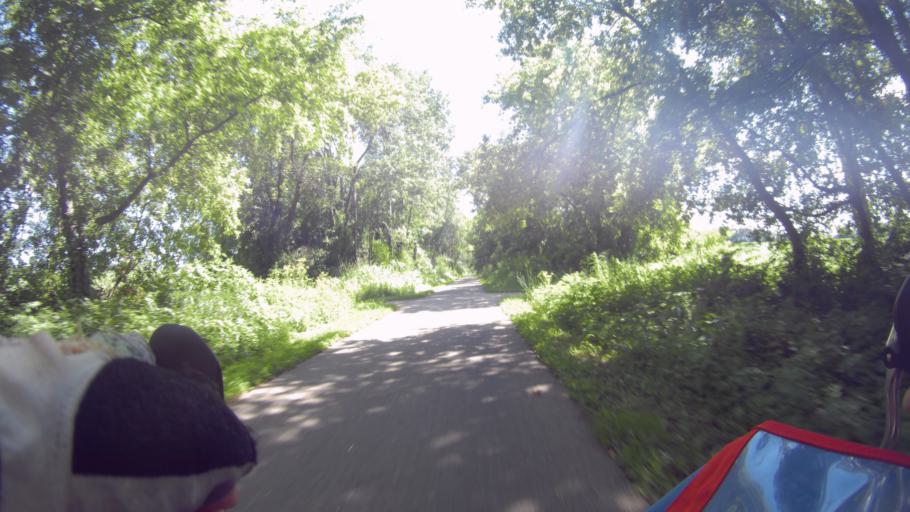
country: US
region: Wisconsin
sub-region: Dane County
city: Fitchburg
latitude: 42.9527
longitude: -89.4745
